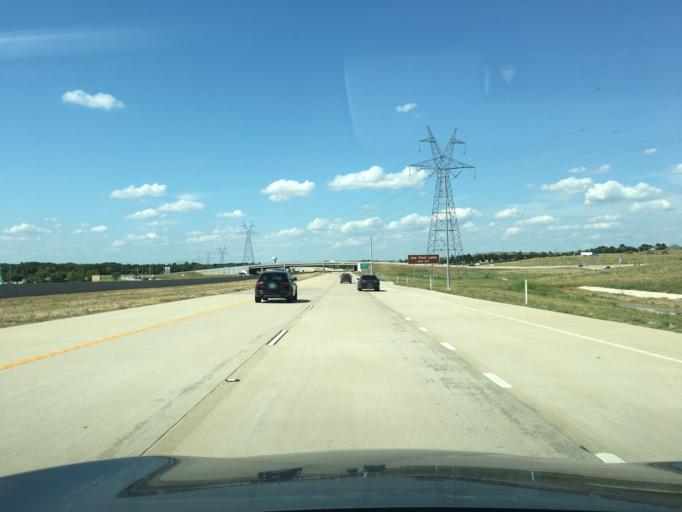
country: US
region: Texas
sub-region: Tarrant County
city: Mansfield
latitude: 32.5781
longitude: -97.0800
